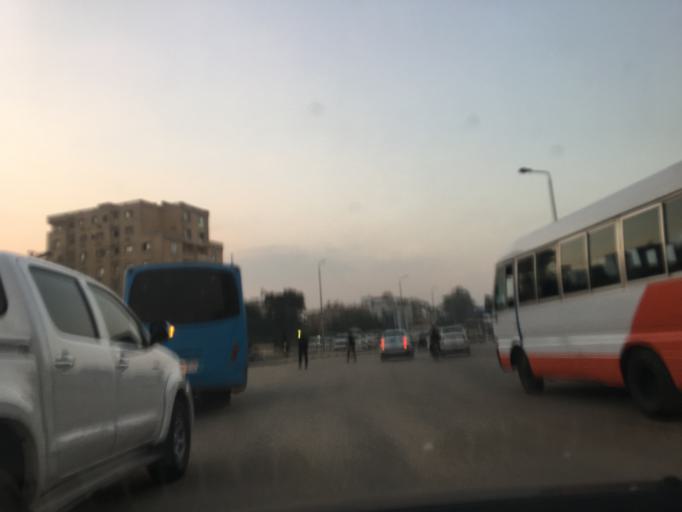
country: EG
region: Al Jizah
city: Al Jizah
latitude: 29.9910
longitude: 31.1313
